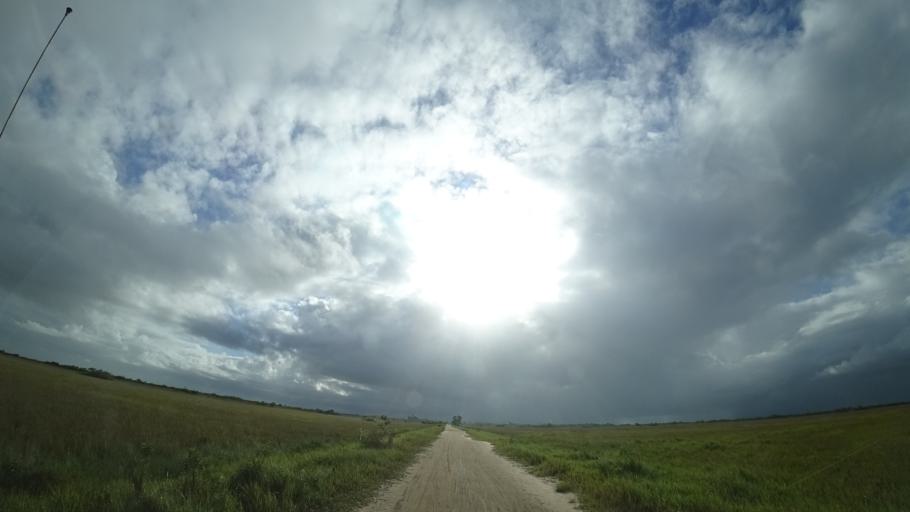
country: MZ
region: Sofala
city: Beira
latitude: -19.6862
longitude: 35.0486
